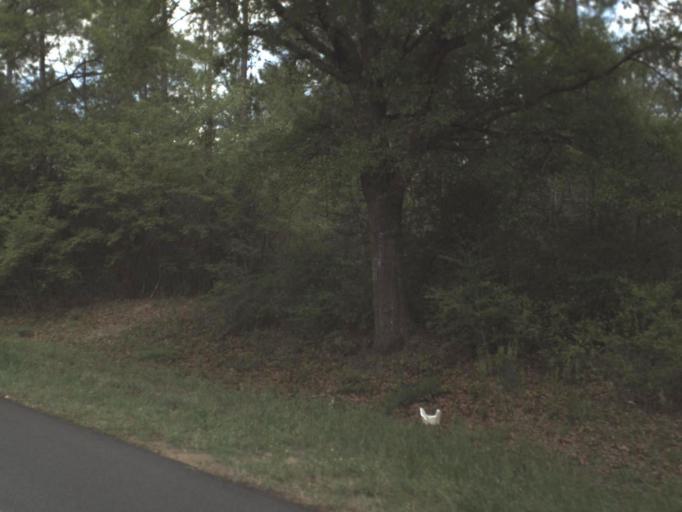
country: US
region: Alabama
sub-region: Covington County
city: Florala
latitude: 30.9439
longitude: -86.4782
